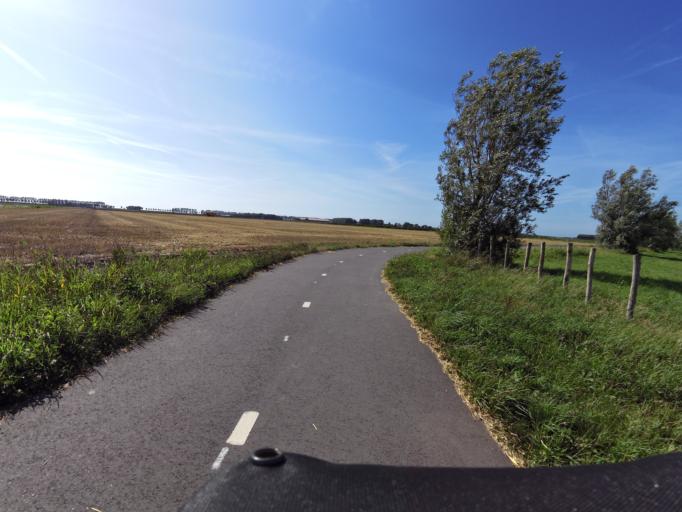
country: NL
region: South Holland
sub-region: Gemeente Goeree-Overflakkee
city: Dirksland
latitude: 51.7394
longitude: 4.0824
